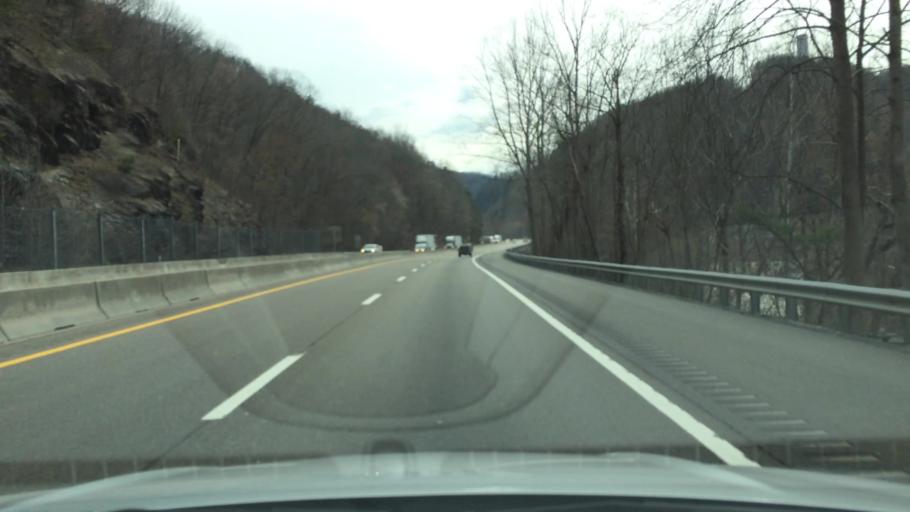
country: US
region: North Carolina
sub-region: Haywood County
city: Cove Creek
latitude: 35.7786
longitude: -83.1037
